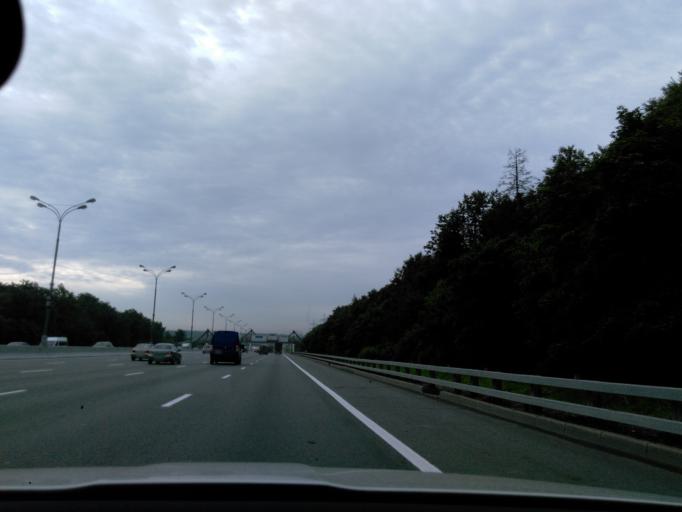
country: RU
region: Moscow
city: Gol'yanovo
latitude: 55.8350
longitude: 37.8176
